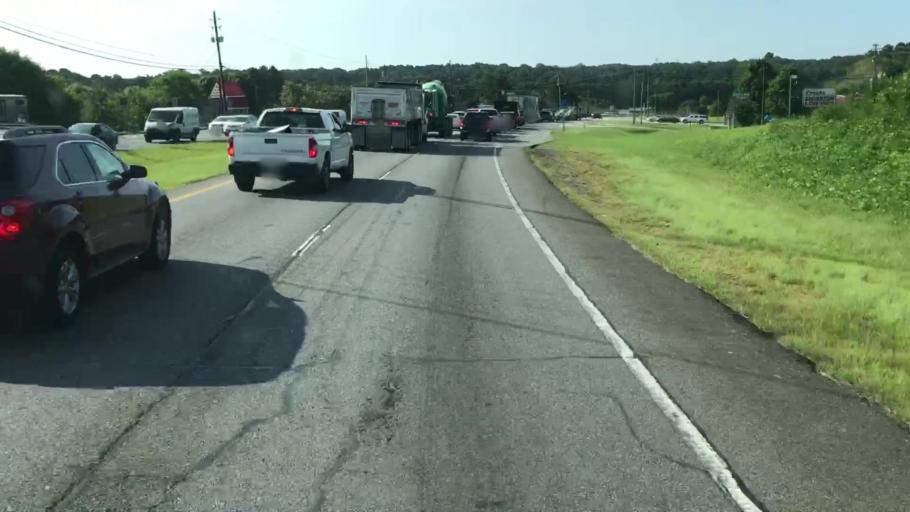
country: US
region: Georgia
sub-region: Gwinnett County
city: Lawrenceville
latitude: 34.0081
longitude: -83.9884
